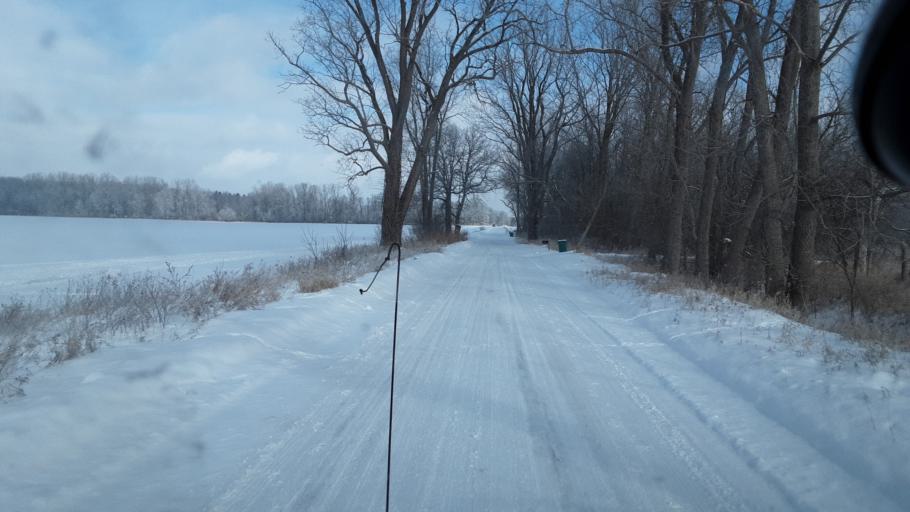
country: US
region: Michigan
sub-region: Eaton County
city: Eaton Rapids
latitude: 42.5148
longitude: -84.6309
